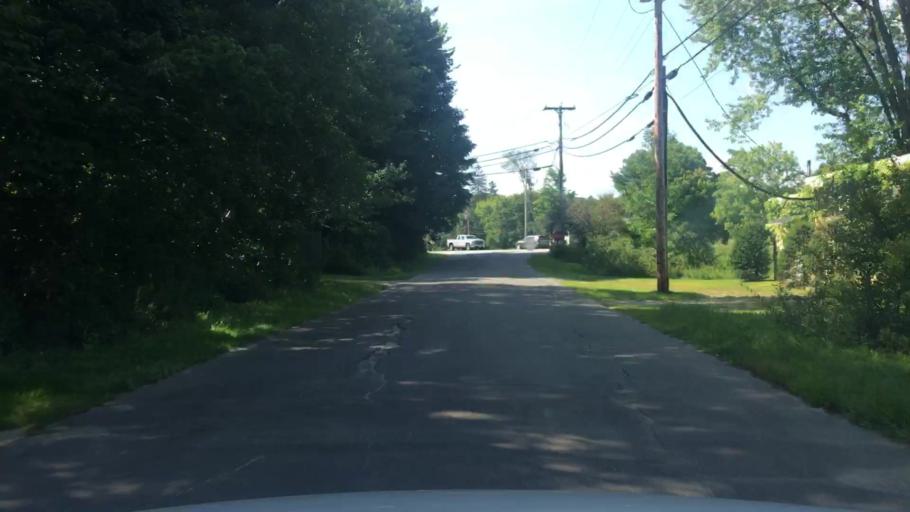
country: US
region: Maine
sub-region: Kennebec County
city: Manchester
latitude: 44.3214
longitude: -69.8957
